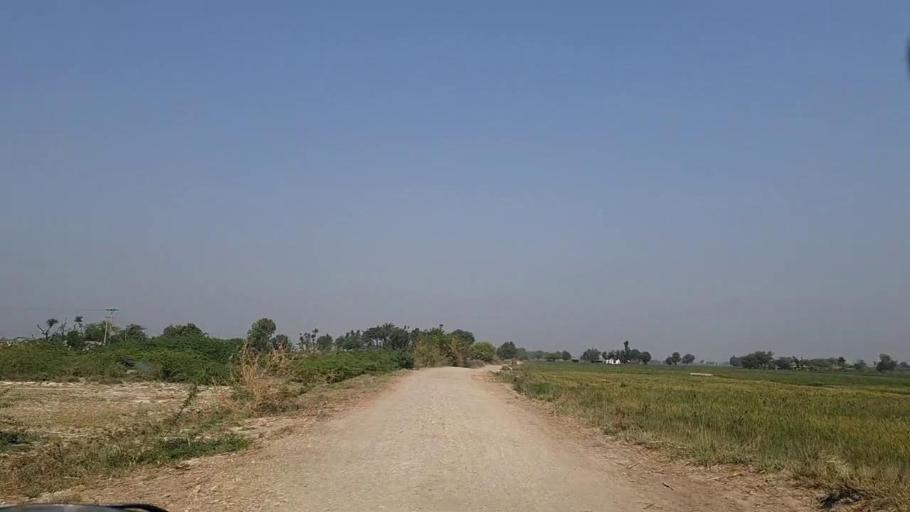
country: PK
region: Sindh
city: Mirpur Khas
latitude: 25.4983
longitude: 69.1909
